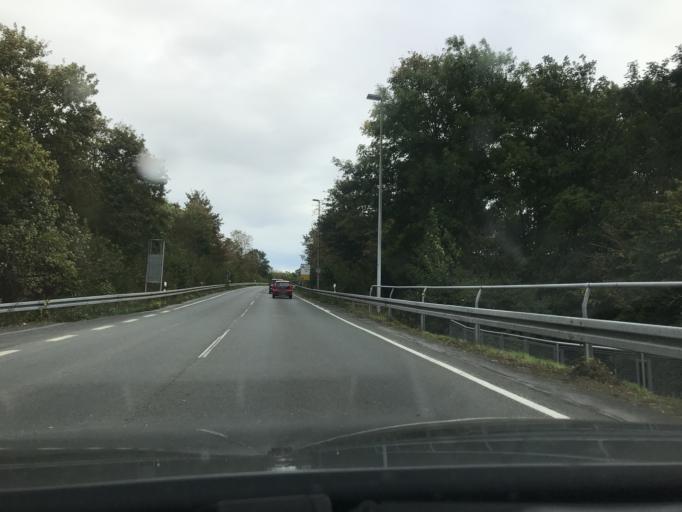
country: DE
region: North Rhine-Westphalia
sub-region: Regierungsbezirk Arnsberg
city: Soest
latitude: 51.5644
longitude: 8.1350
